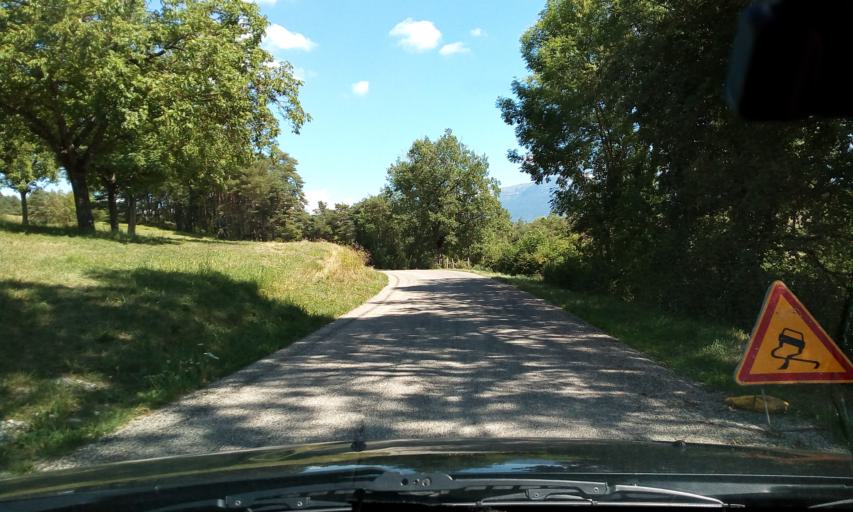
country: FR
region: Rhone-Alpes
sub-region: Departement de l'Isere
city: Mens
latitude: 44.7755
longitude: 5.6678
